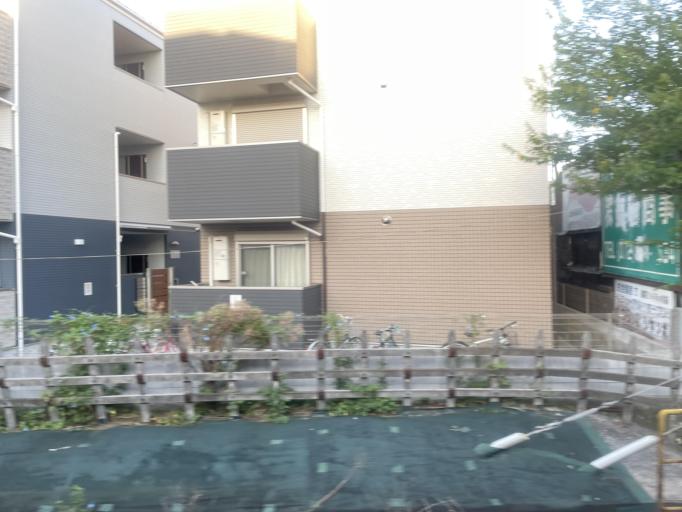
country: JP
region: Osaka
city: Matsubara
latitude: 34.5892
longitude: 135.5343
